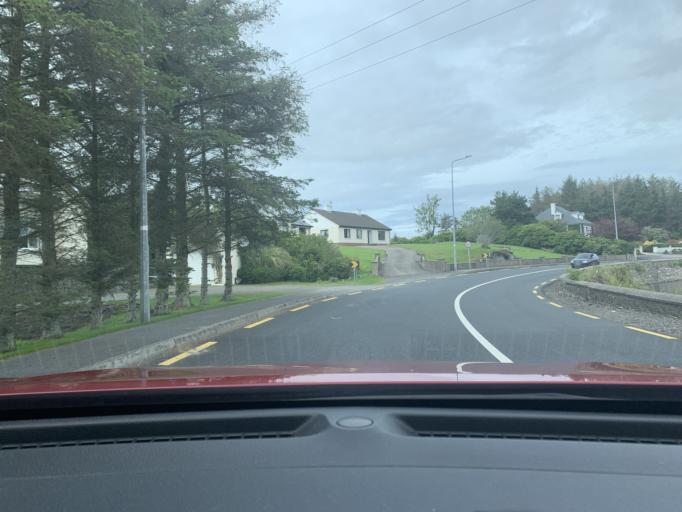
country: IE
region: Ulster
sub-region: County Donegal
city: Dungloe
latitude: 54.9484
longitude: -8.3417
